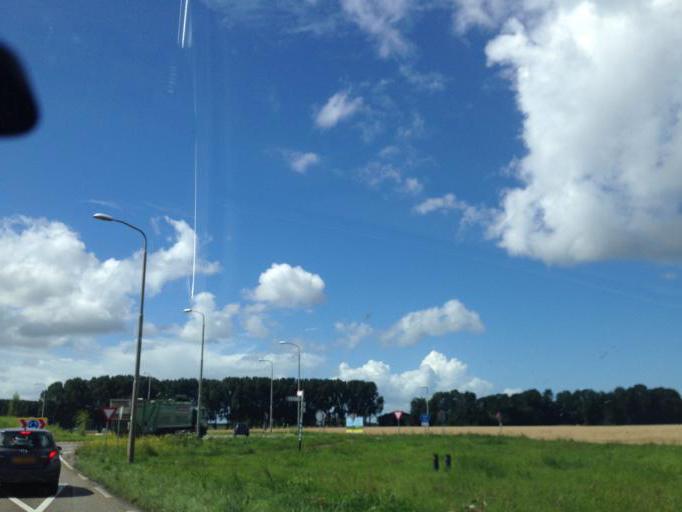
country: NL
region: Flevoland
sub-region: Gemeente Dronten
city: Dronten
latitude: 52.5378
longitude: 5.7407
